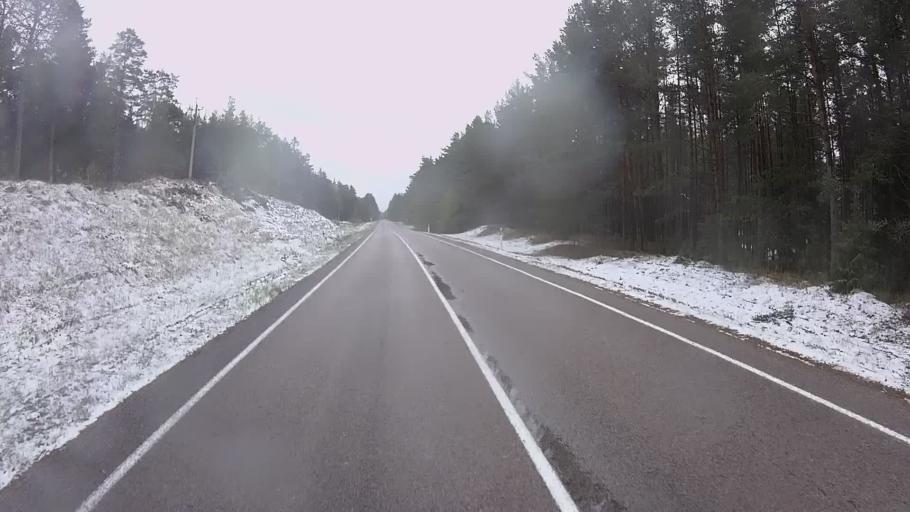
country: EE
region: Hiiumaa
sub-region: Kaerdla linn
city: Kardla
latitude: 58.8537
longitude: 22.4642
